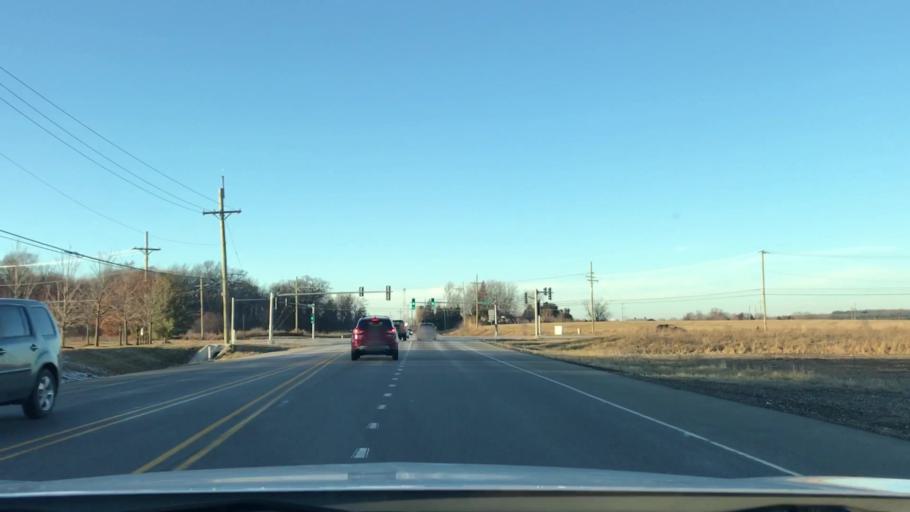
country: US
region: Illinois
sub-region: Kane County
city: Gilberts
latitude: 42.0967
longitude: -88.4017
